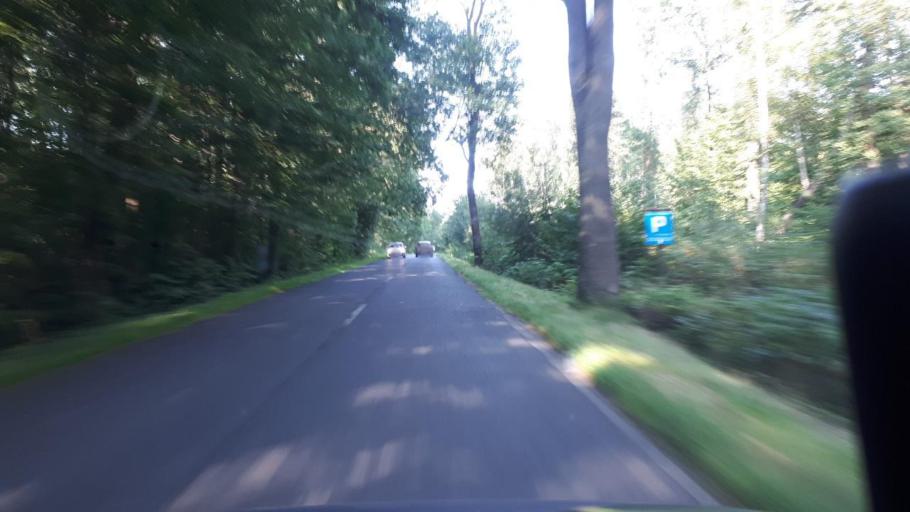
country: PL
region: Silesian Voivodeship
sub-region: Powiat tarnogorski
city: Tworog
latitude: 50.4788
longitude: 18.6857
